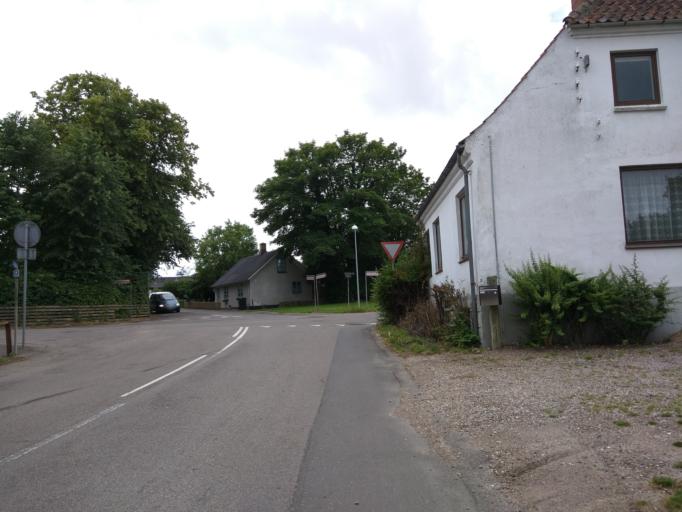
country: DK
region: Zealand
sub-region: Kalundborg Kommune
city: Svebolle
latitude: 55.7133
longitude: 11.3021
